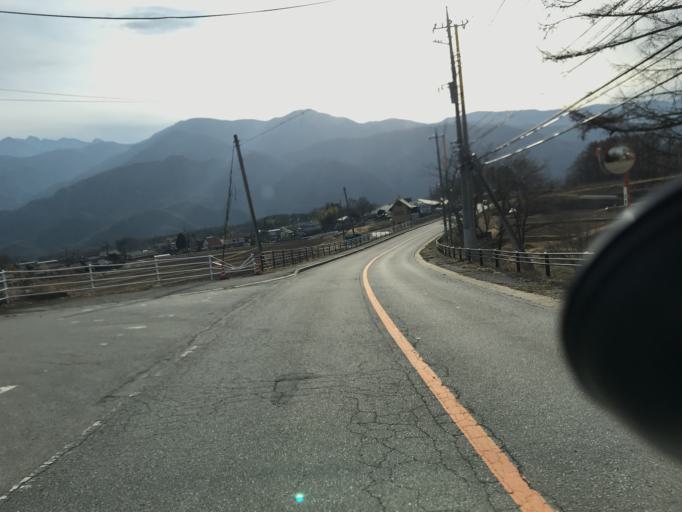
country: JP
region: Nagano
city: Chino
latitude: 35.8670
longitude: 138.3065
